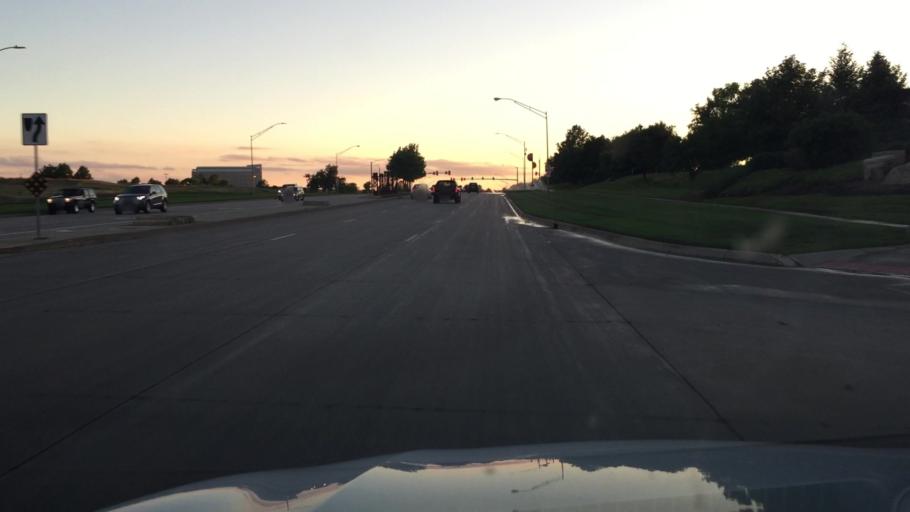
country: US
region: Iowa
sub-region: Polk County
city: Clive
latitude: 41.5619
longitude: -93.8001
